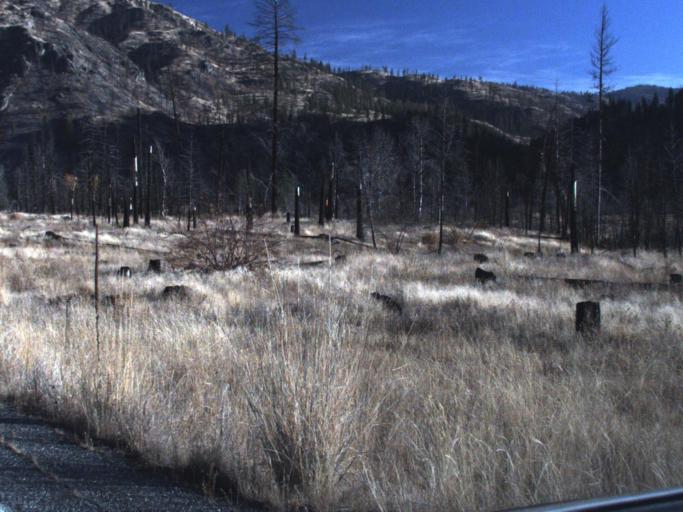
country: US
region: Washington
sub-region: Ferry County
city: Republic
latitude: 48.2558
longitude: -118.6915
